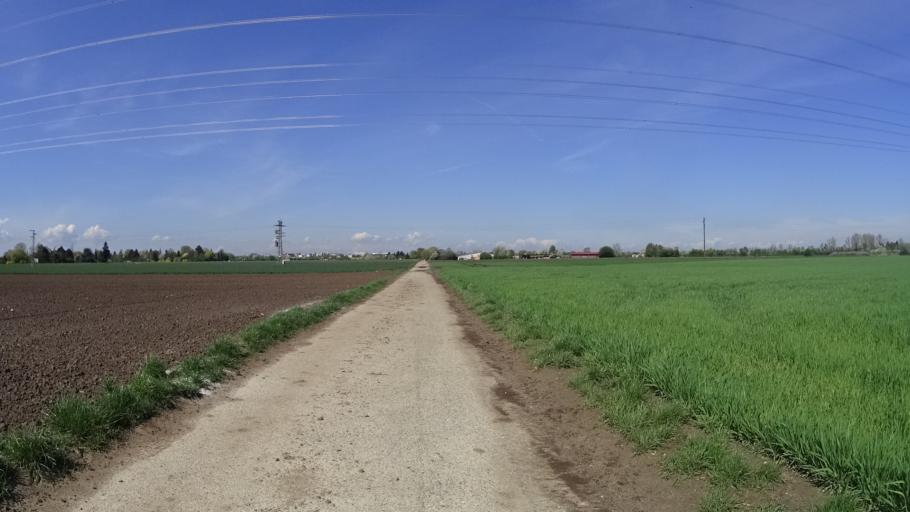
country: DE
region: Baden-Wuerttemberg
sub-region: Karlsruhe Region
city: Heddesheim
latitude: 49.5364
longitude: 8.6160
